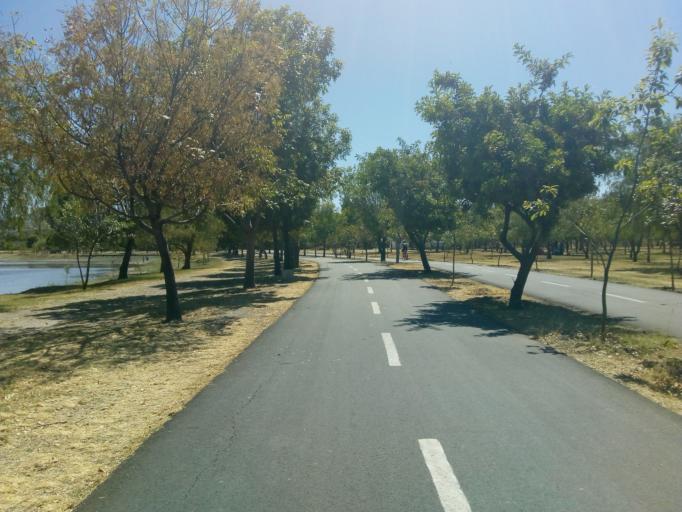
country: MX
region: Guanajuato
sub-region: Leon
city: La Ermita
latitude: 21.1859
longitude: -101.6937
